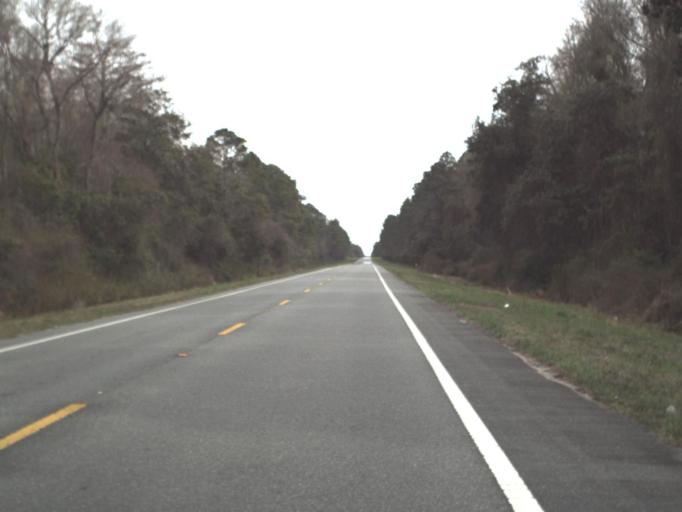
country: US
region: Florida
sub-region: Wakulla County
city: Crawfordville
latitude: 30.3212
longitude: -84.4522
